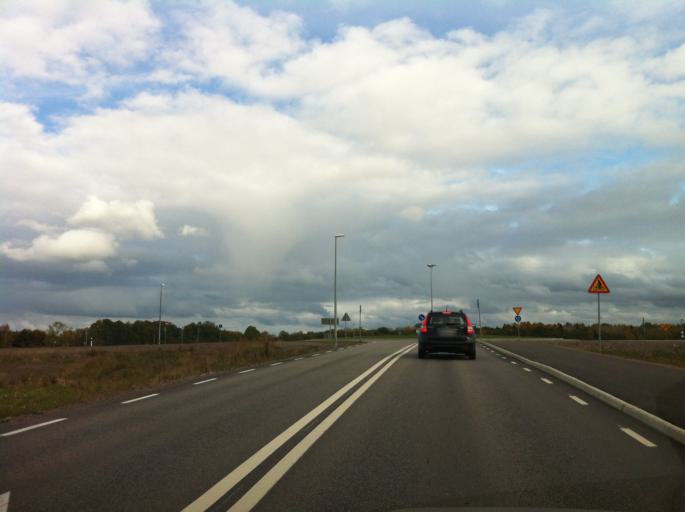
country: SE
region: OEstergoetland
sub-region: Motala Kommun
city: Motala
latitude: 58.5049
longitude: 15.0181
